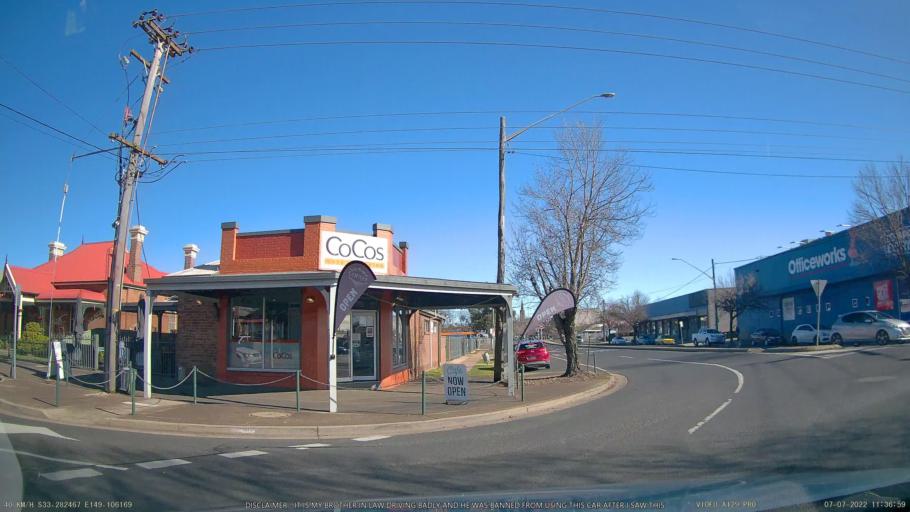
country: AU
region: New South Wales
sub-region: Orange Municipality
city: Orange
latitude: -33.2825
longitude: 149.1059
